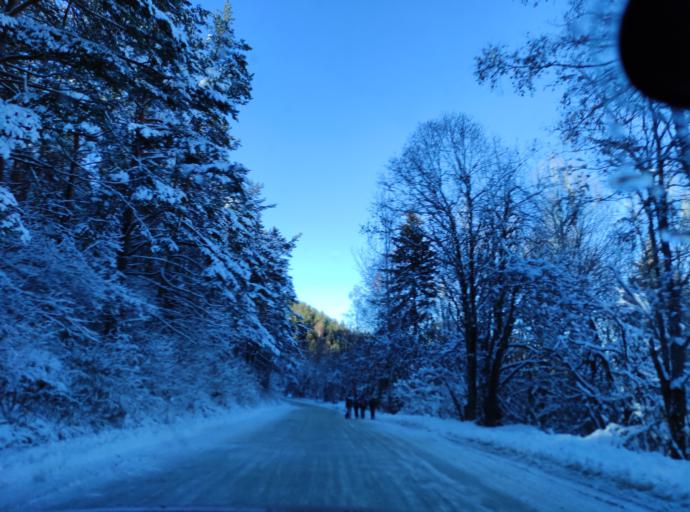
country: BG
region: Sofia-Capital
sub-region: Stolichna Obshtina
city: Sofia
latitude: 42.5983
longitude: 23.3054
